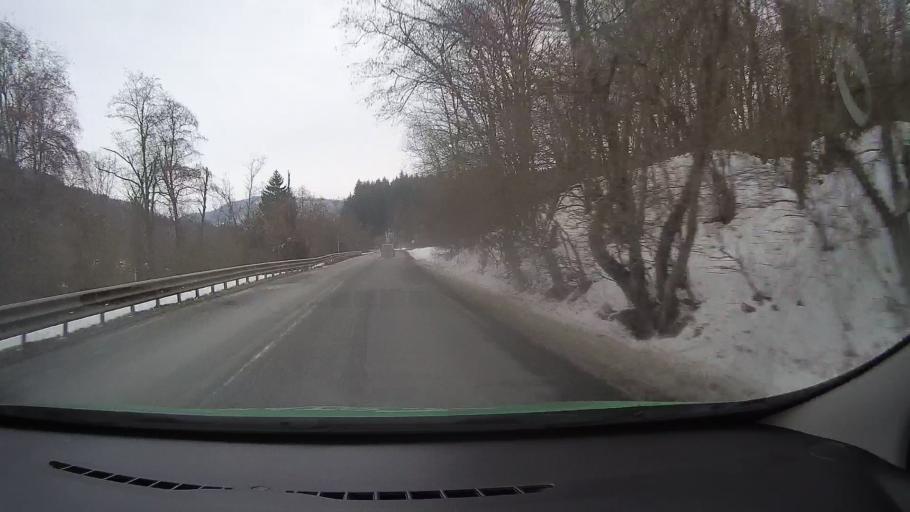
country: RO
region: Brasov
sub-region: Oras Predeal
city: Predeal
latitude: 45.5265
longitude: 25.5011
